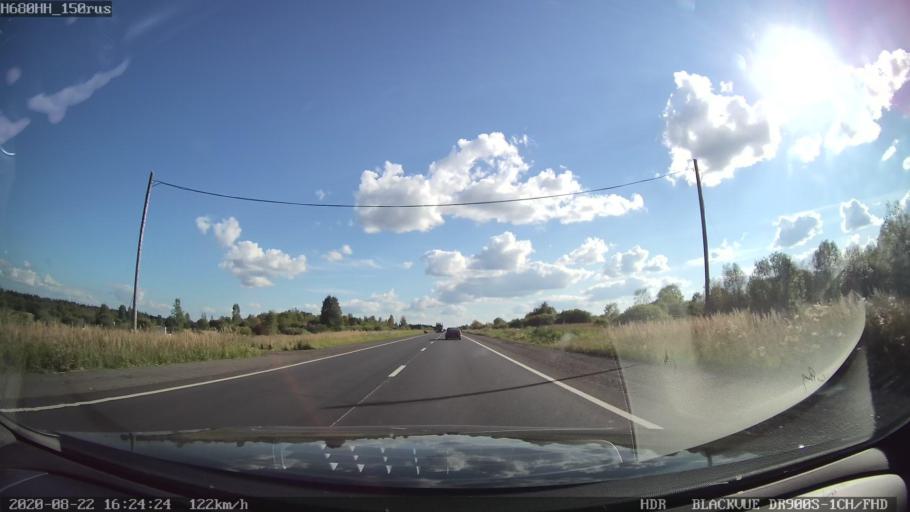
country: RU
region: Tverskaya
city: Rameshki
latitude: 57.3375
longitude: 36.0953
